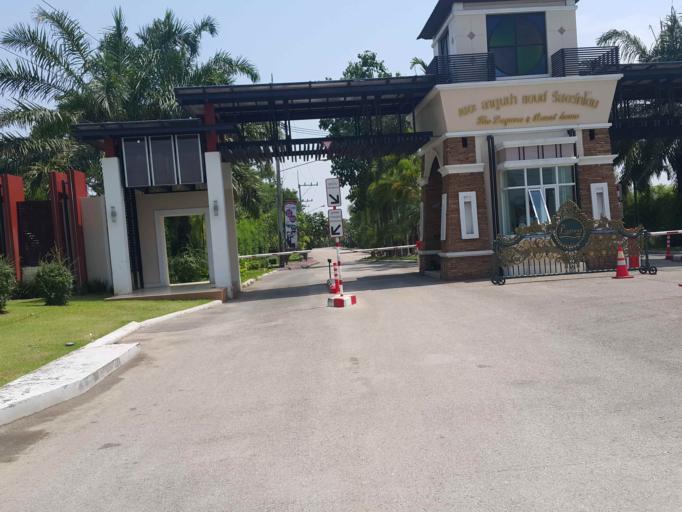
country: TH
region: Chiang Mai
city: San Sai
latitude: 18.8377
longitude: 99.0279
